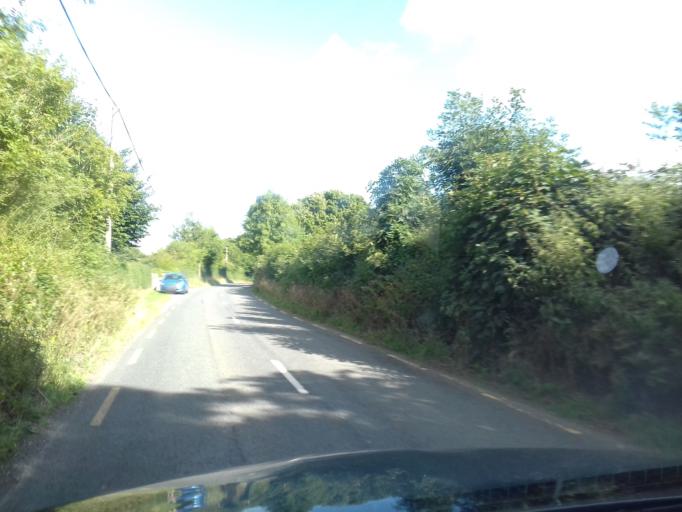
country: IE
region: Leinster
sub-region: Kilkenny
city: Graiguenamanagh
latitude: 52.5485
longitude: -7.0429
